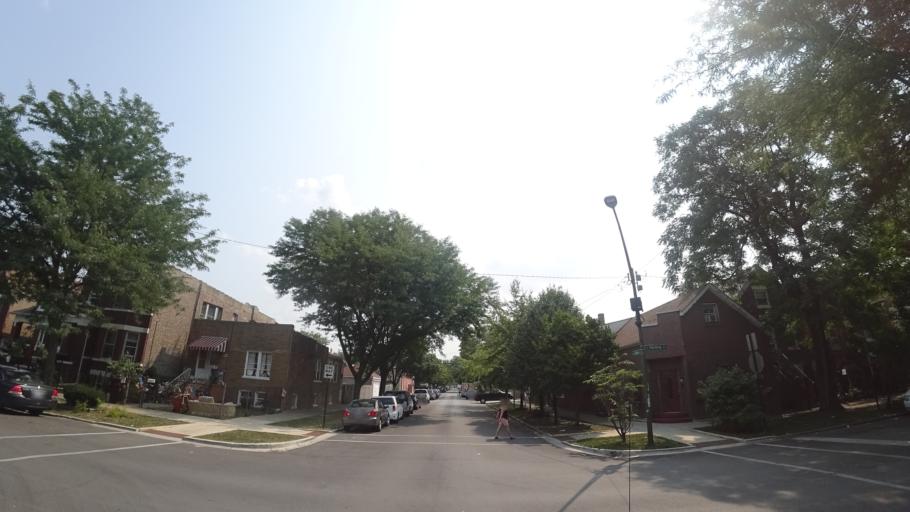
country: US
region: Illinois
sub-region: Cook County
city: Cicero
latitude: 41.8387
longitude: -87.7233
